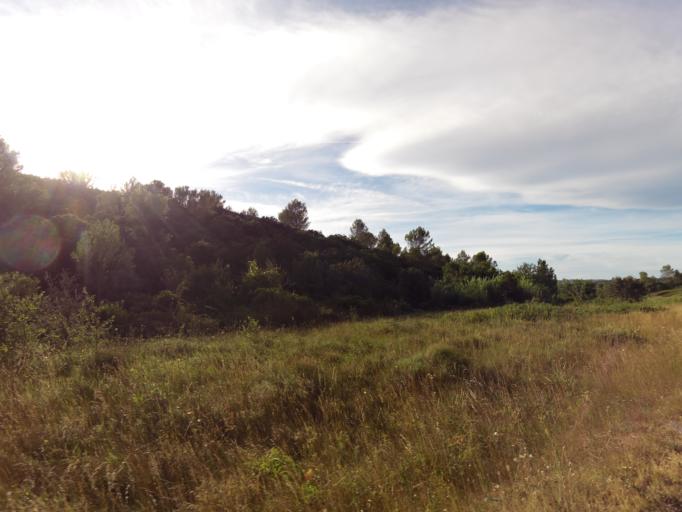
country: FR
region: Languedoc-Roussillon
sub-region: Departement du Gard
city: Congenies
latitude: 43.8138
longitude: 4.1479
